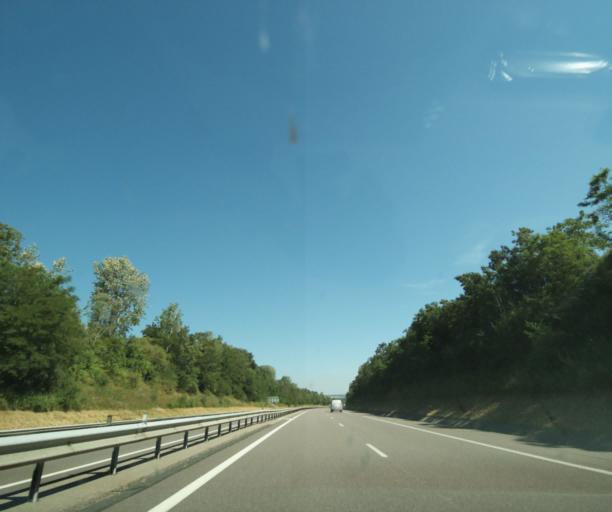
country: FR
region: Lorraine
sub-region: Departement des Vosges
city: Chatenois
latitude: 48.2804
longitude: 5.8557
